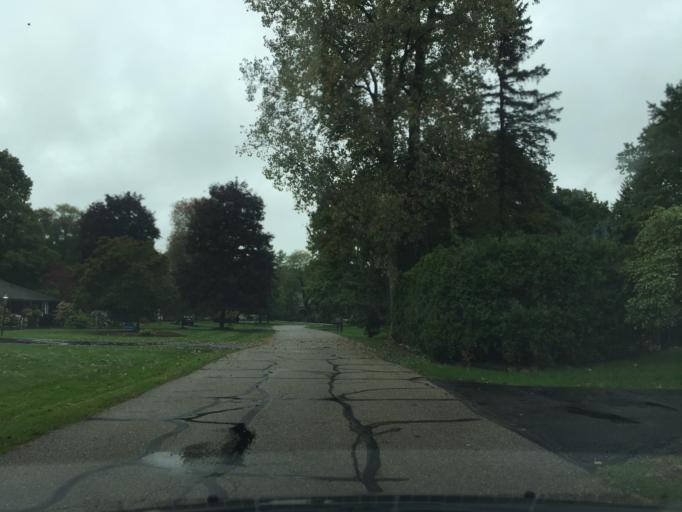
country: US
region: Michigan
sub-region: Oakland County
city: Bingham Farms
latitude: 42.5382
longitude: -83.2768
